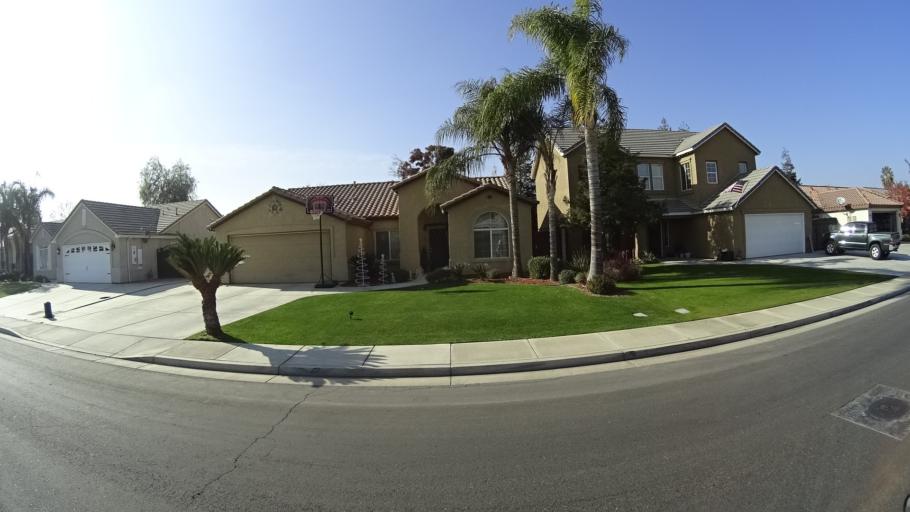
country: US
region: California
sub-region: Kern County
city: Rosedale
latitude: 35.3573
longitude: -119.1648
